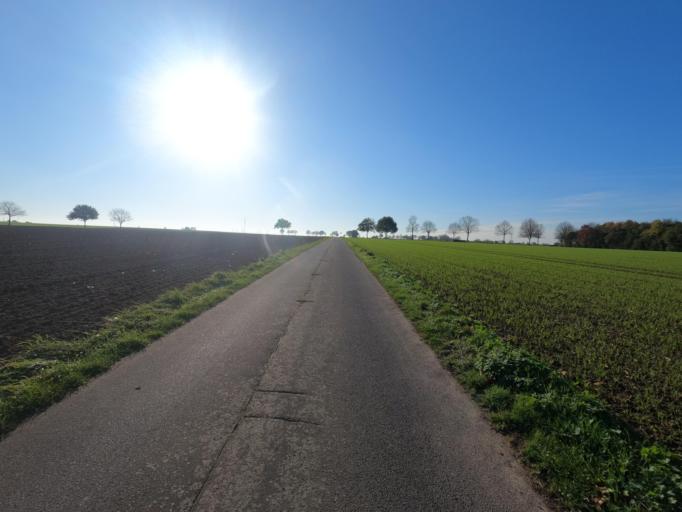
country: DE
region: North Rhine-Westphalia
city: Erkelenz
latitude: 51.0897
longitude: 6.3504
